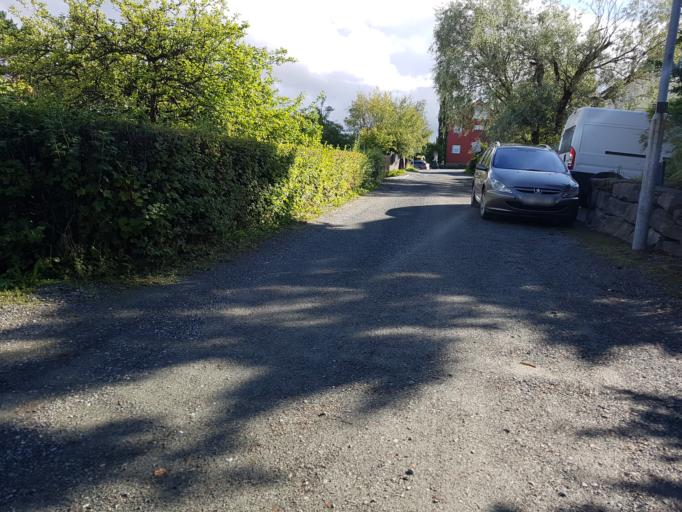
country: NO
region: Sor-Trondelag
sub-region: Trondheim
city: Trondheim
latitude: 63.4280
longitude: 10.4414
